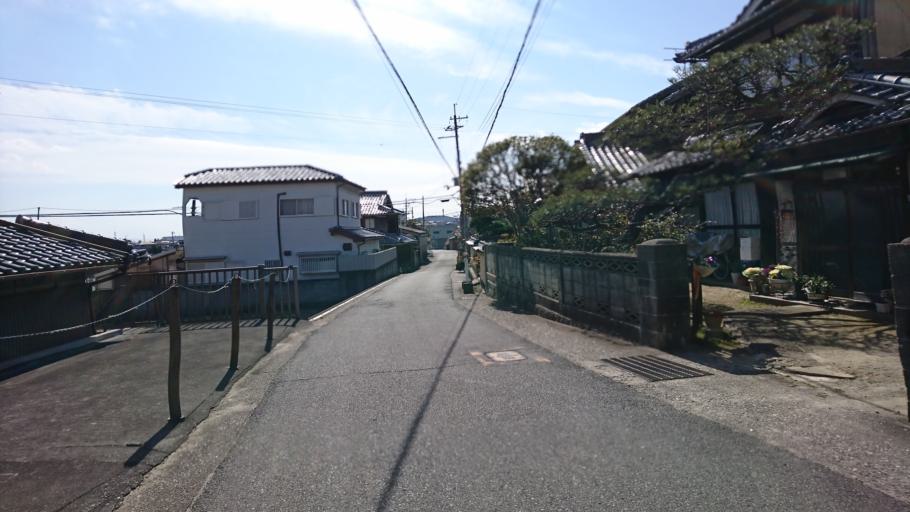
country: JP
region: Hyogo
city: Kakogawacho-honmachi
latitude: 34.7995
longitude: 134.8090
